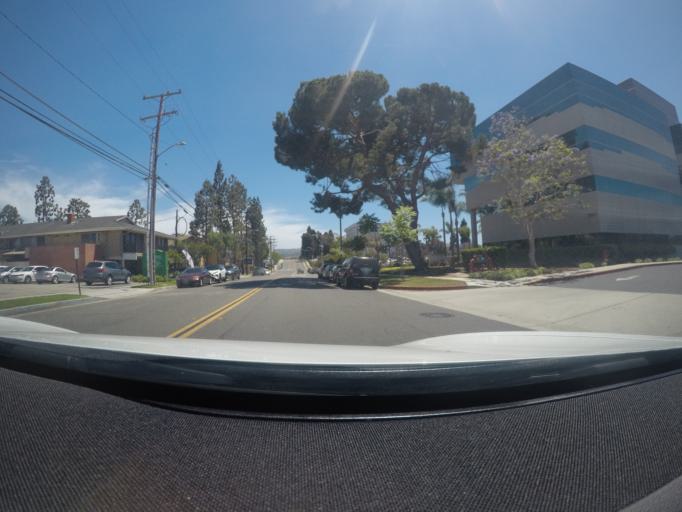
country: US
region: California
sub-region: Los Angeles County
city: Torrance
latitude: 33.8408
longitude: -118.3581
